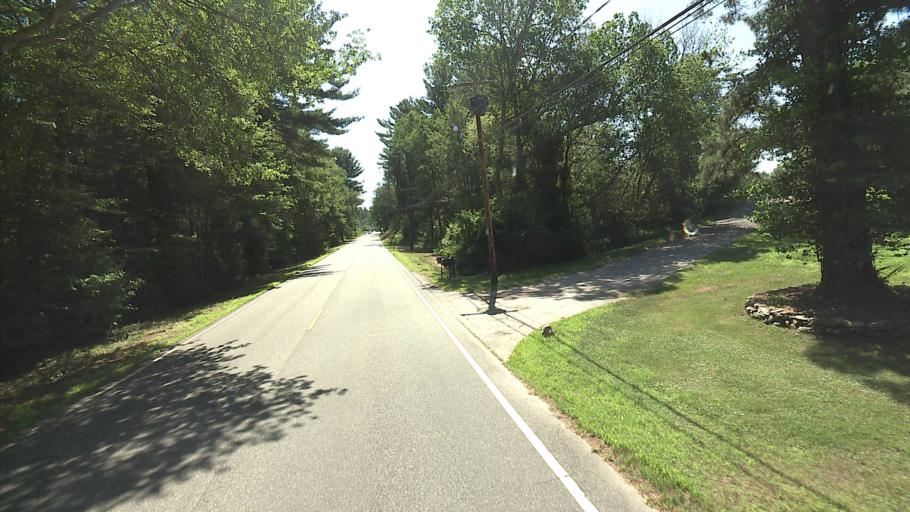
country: US
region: Connecticut
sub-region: Windham County
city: Moosup
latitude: 41.7002
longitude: -71.7979
